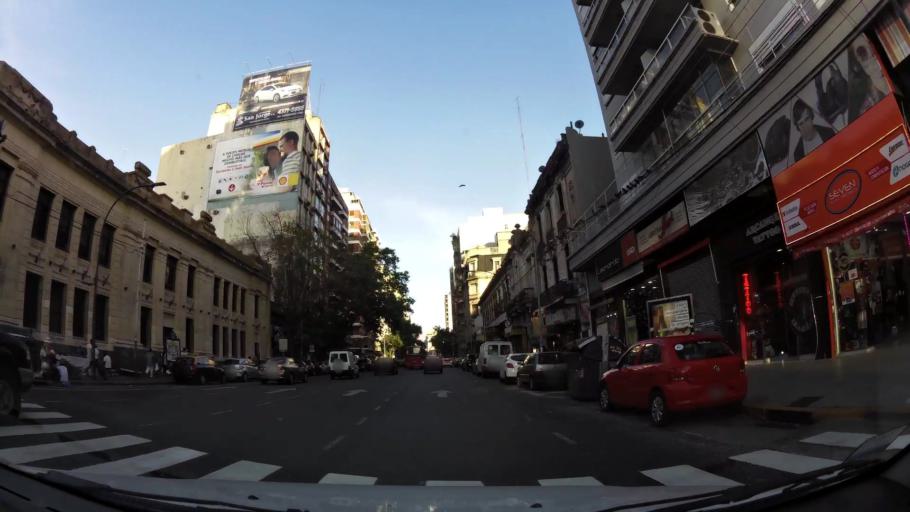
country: AR
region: Buenos Aires F.D.
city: Buenos Aires
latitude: -34.6041
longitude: -58.4088
